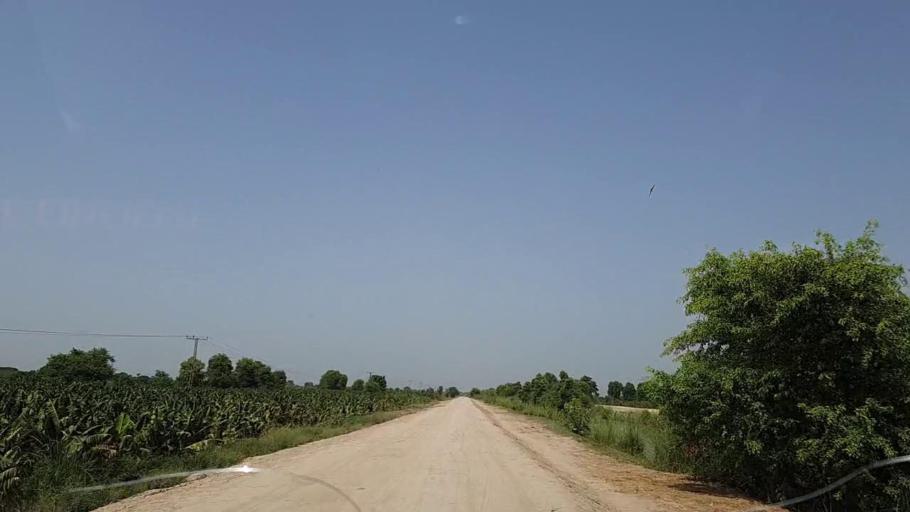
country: PK
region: Sindh
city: Kandiaro
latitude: 27.0363
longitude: 68.1508
